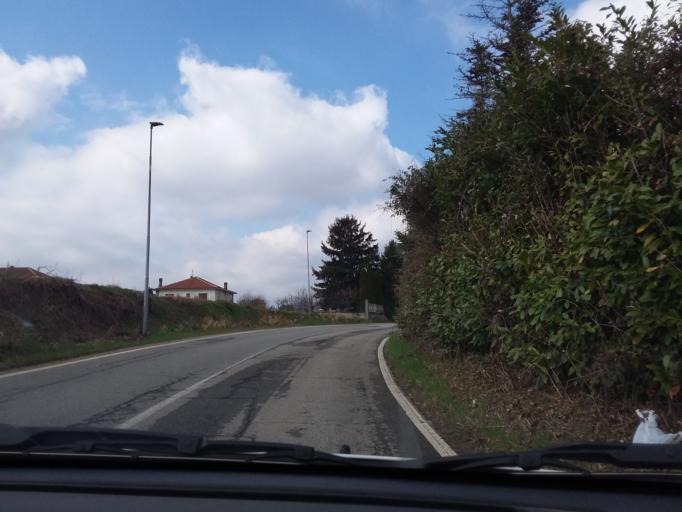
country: IT
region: Piedmont
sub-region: Provincia di Torino
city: Tetti Neirotti
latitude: 45.0559
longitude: 7.5311
